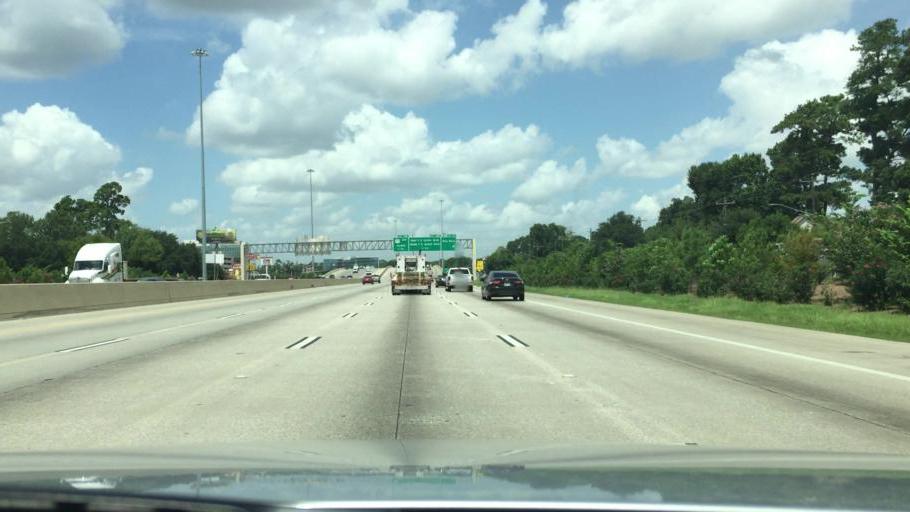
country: US
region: Texas
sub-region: Harris County
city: Houston
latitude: 29.8125
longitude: -95.4237
